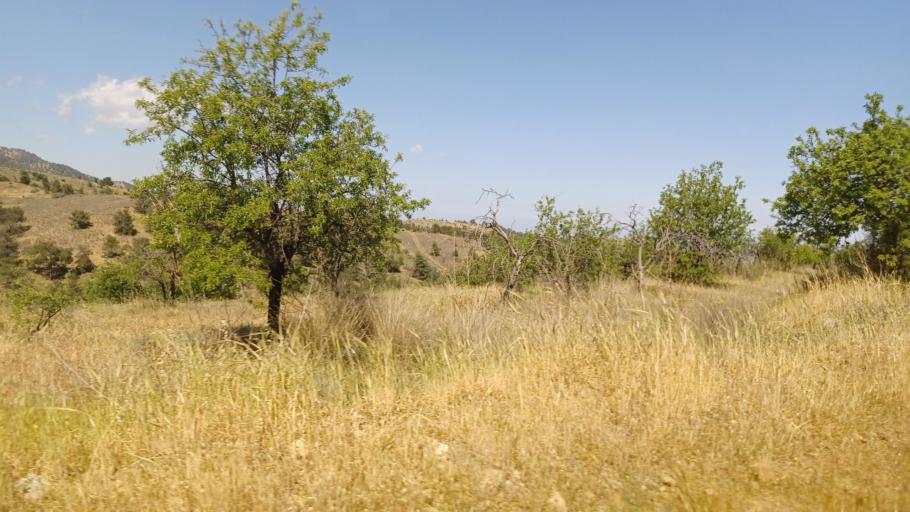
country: CY
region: Lefkosia
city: Astromeritis
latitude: 35.0589
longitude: 33.0235
